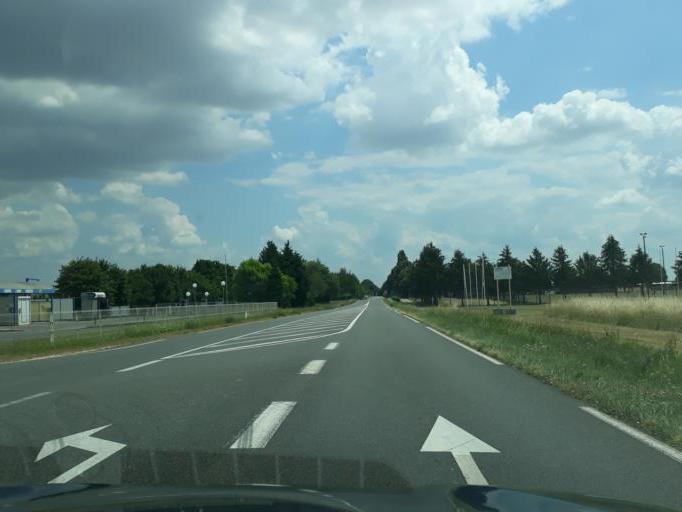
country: FR
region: Centre
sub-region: Departement du Cher
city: Avord
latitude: 47.0318
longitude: 2.6451
